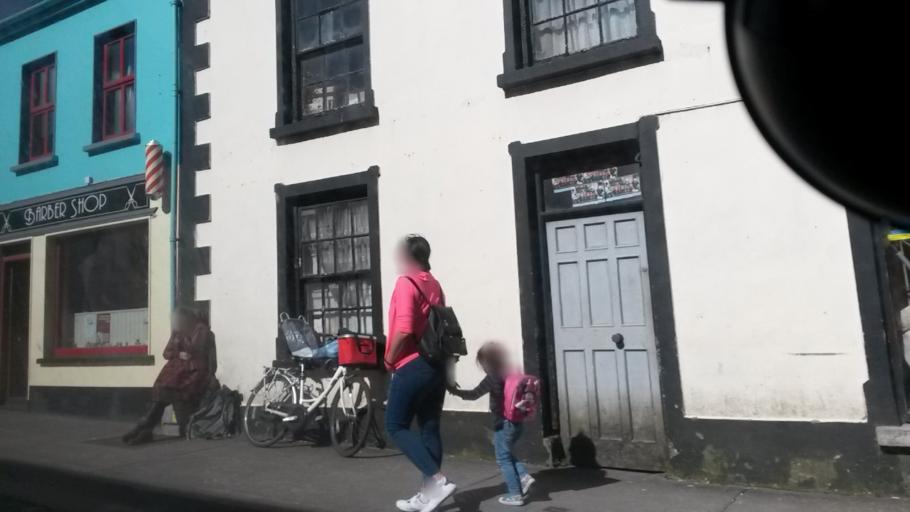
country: IE
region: Munster
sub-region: Ciarrai
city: Dingle
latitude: 52.1410
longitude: -10.2673
